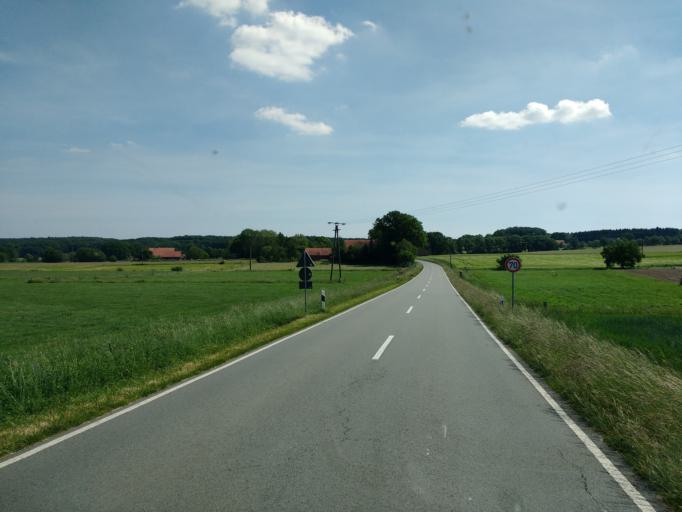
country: DE
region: Lower Saxony
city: Belm
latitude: 52.3734
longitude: 8.1039
